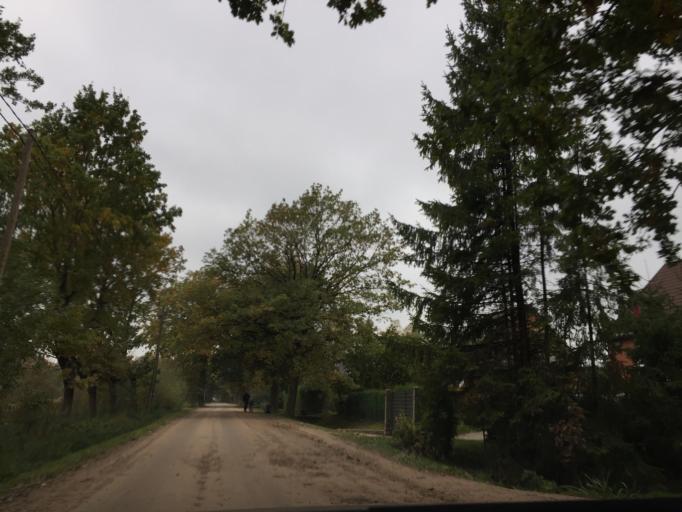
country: LV
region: Jelgava
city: Jelgava
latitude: 56.6845
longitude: 23.7281
